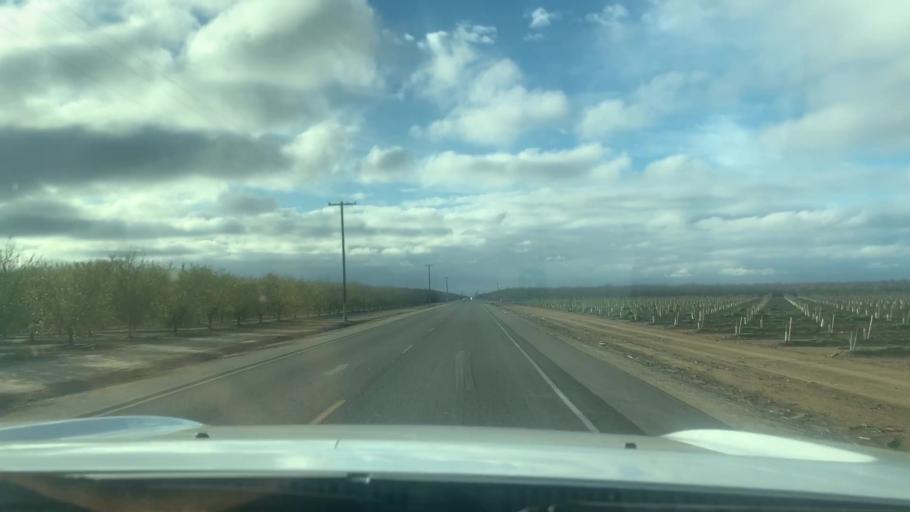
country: US
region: California
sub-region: Kern County
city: Wasco
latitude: 35.5002
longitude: -119.3870
